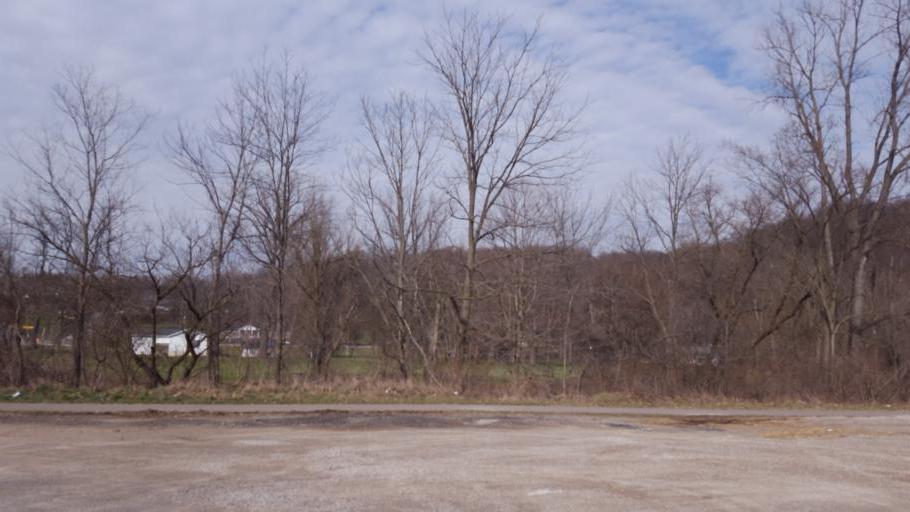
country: US
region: Ohio
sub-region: Sandusky County
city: Bellville
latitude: 40.6222
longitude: -82.5091
